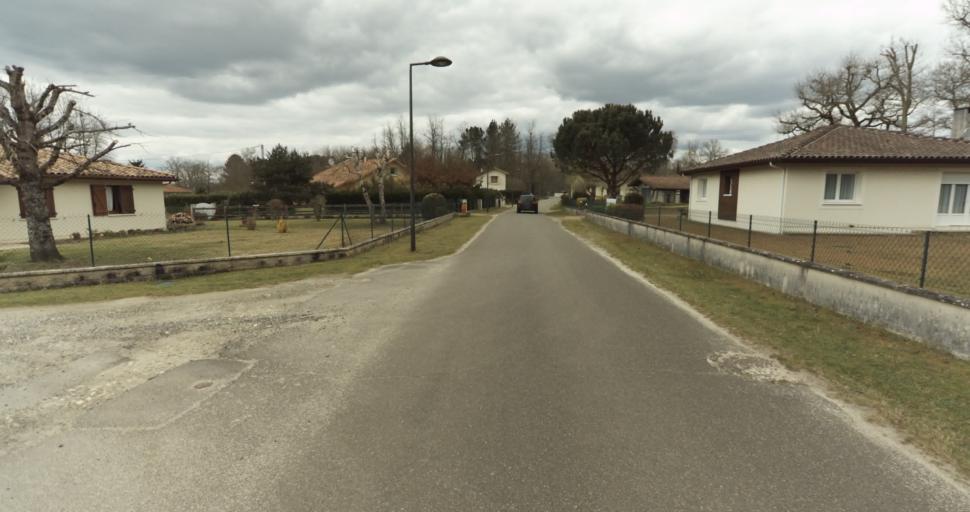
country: FR
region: Aquitaine
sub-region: Departement des Landes
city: Roquefort
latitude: 44.0353
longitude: -0.3096
